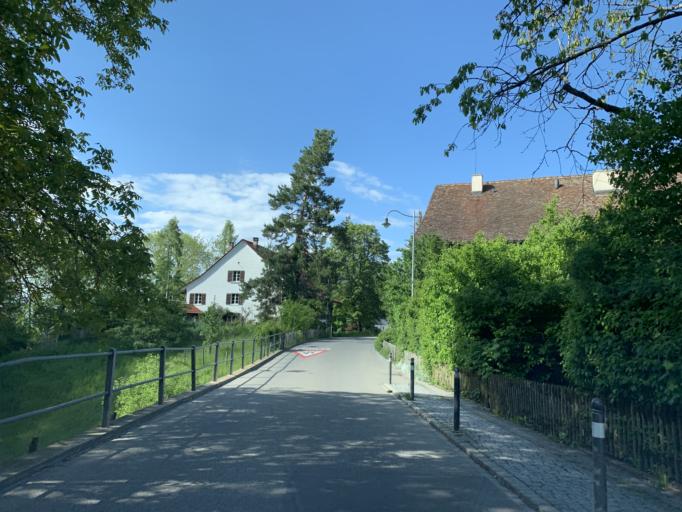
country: CH
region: Zurich
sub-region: Bezirk Winterthur
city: Kollbrunn / Kollbrunn (Dorfkern)
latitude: 47.4557
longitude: 8.7434
